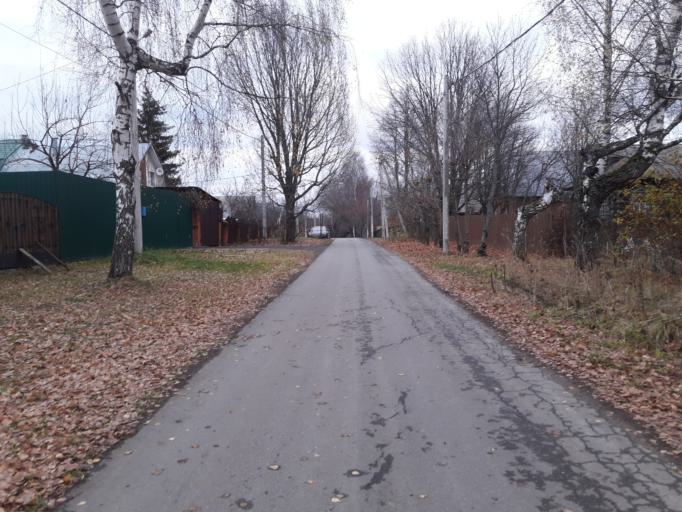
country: RU
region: Moskovskaya
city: Sofrino
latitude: 56.1707
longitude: 37.9290
